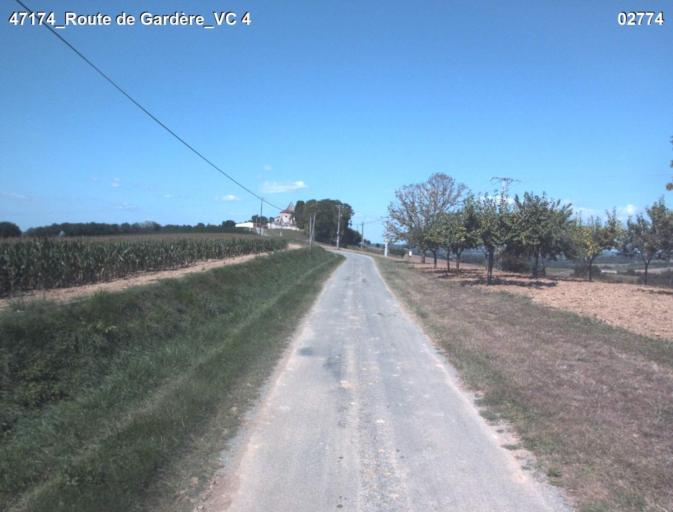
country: FR
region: Midi-Pyrenees
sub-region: Departement du Gers
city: Condom
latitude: 44.0409
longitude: 0.4114
